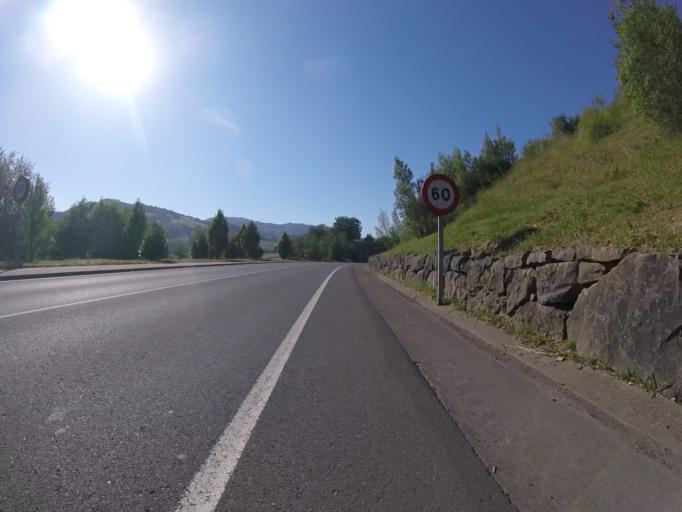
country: ES
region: Basque Country
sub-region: Provincia de Guipuzcoa
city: Azpeitia
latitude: 43.1749
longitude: -2.2589
